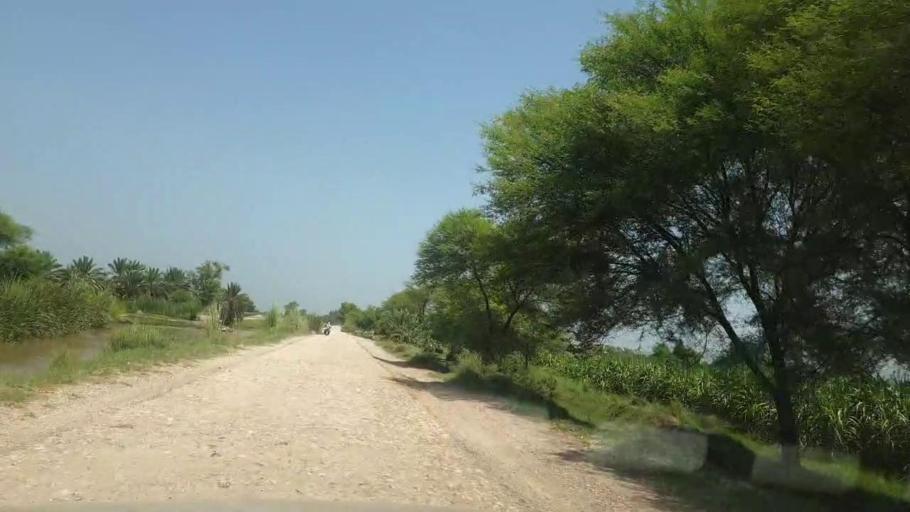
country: PK
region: Sindh
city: Pano Aqil
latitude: 27.6598
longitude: 69.1073
